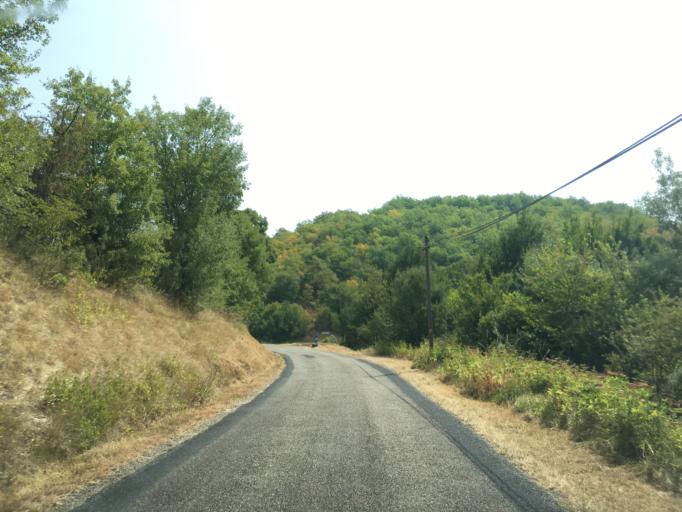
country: FR
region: Midi-Pyrenees
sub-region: Departement du Lot
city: Le Vigan
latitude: 44.7429
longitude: 1.5186
